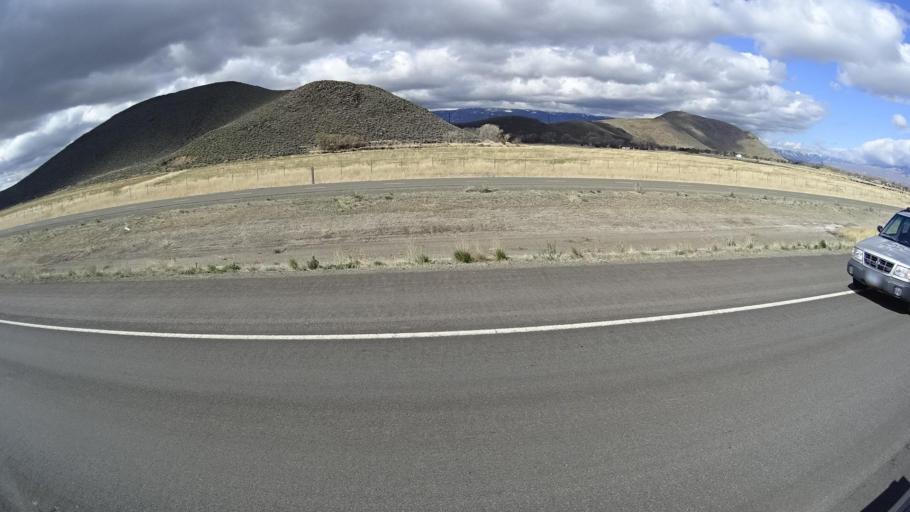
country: US
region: Nevada
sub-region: Washoe County
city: Sparks
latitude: 39.4721
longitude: -119.7346
